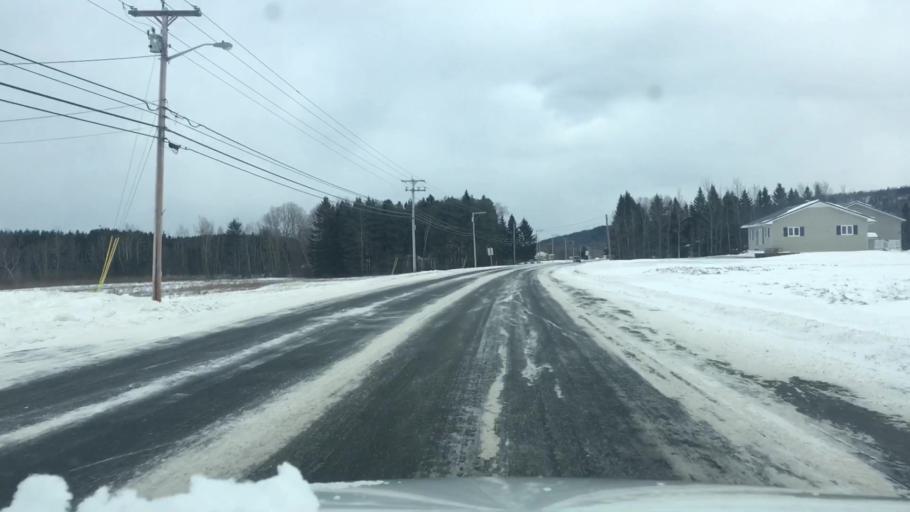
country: US
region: Maine
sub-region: Aroostook County
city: Madawaska
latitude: 47.3433
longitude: -68.2405
